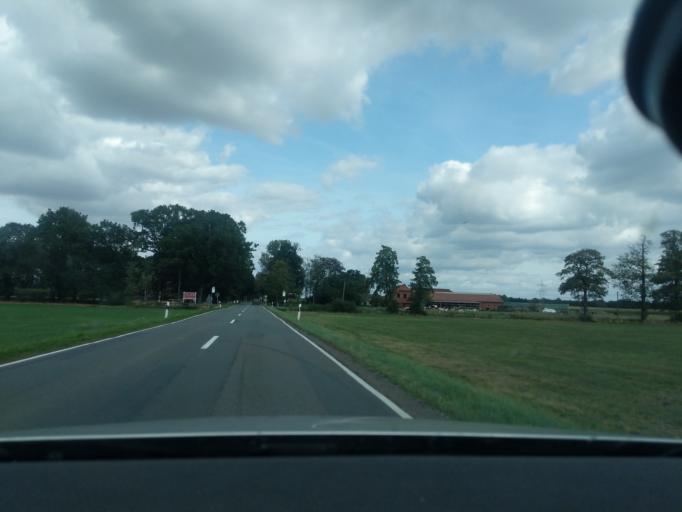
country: DE
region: Lower Saxony
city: Warpe
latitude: 52.7612
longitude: 9.0893
